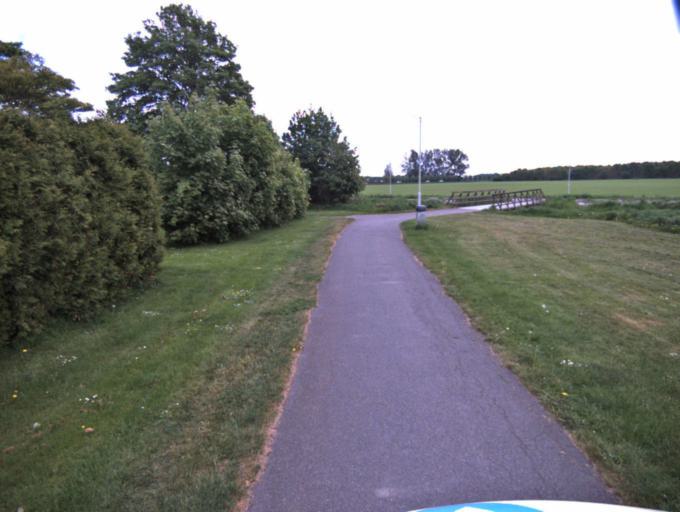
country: SE
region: Skane
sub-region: Kristianstads Kommun
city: Kristianstad
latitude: 56.0087
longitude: 14.1472
